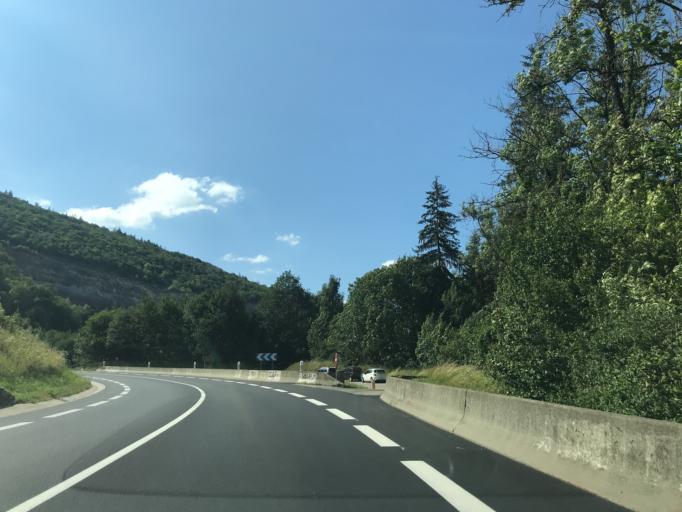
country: FR
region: Rhone-Alpes
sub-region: Departement de la Haute-Savoie
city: Dingy-Saint-Clair
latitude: 45.9074
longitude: 6.2033
